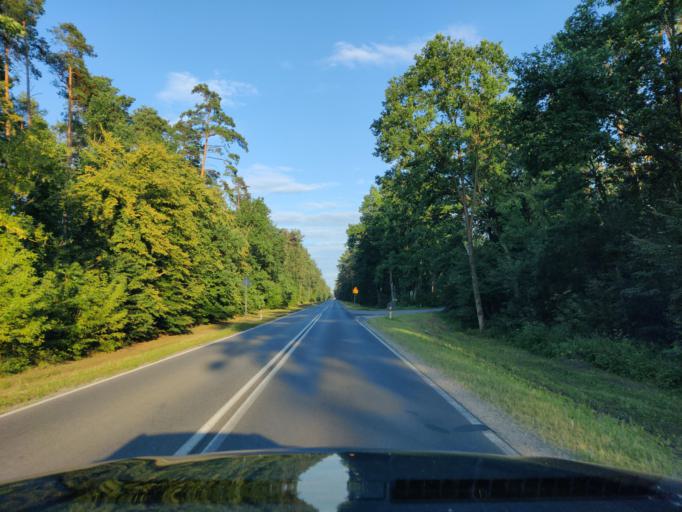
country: PL
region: Masovian Voivodeship
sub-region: Powiat pultuski
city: Pultusk
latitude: 52.6810
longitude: 21.1285
